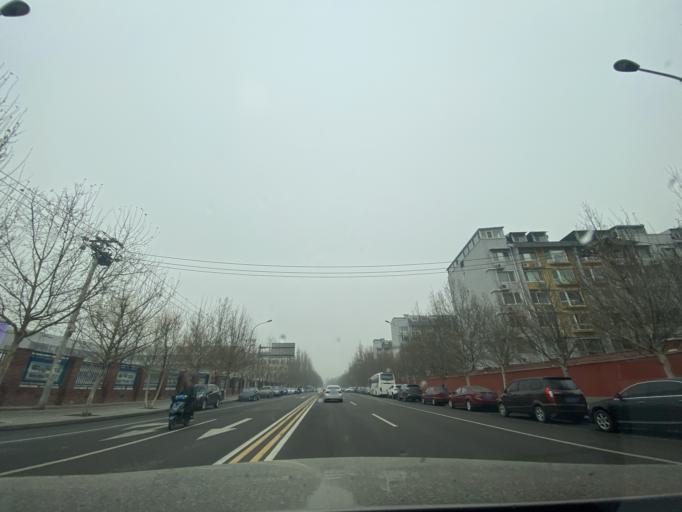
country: CN
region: Beijing
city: Sijiqing
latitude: 39.9626
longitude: 116.2419
